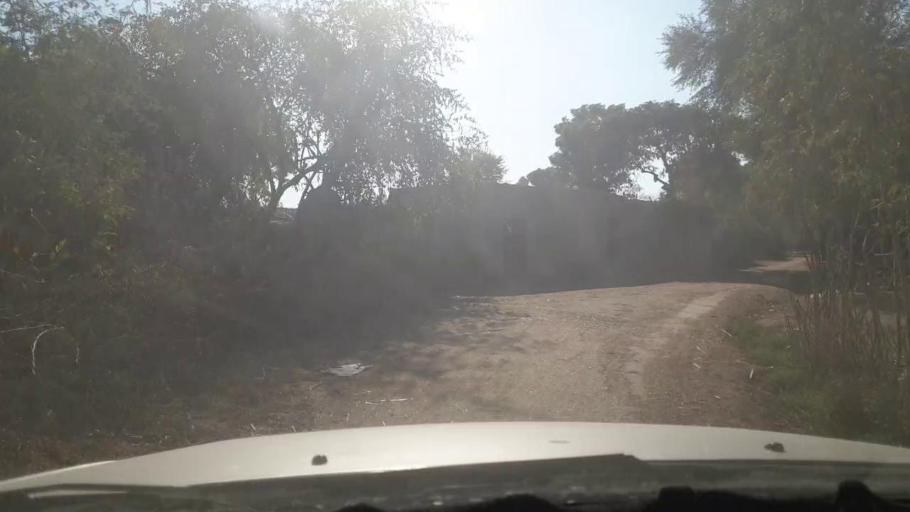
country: PK
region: Sindh
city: Ghotki
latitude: 27.9739
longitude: 69.1867
